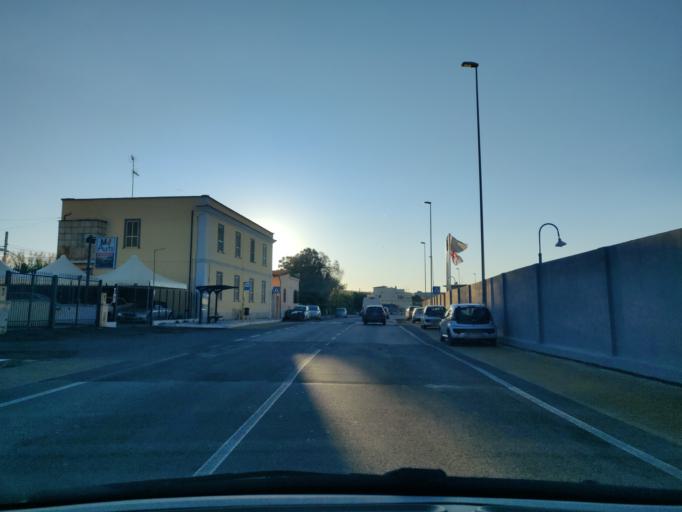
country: IT
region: Latium
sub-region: Citta metropolitana di Roma Capitale
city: Civitavecchia
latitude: 42.1076
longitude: 11.7804
